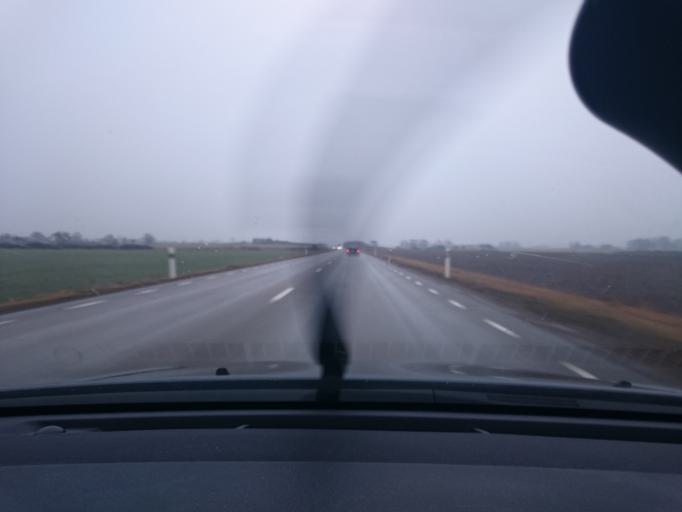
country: SE
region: Skane
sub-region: Bastads Kommun
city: Forslov
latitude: 56.3300
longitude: 12.8191
